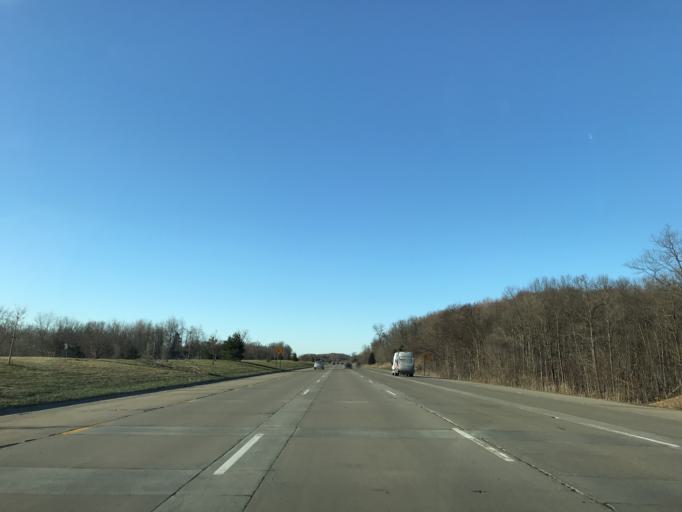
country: US
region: Michigan
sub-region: Oakland County
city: Walled Lake
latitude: 42.5254
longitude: -83.4457
